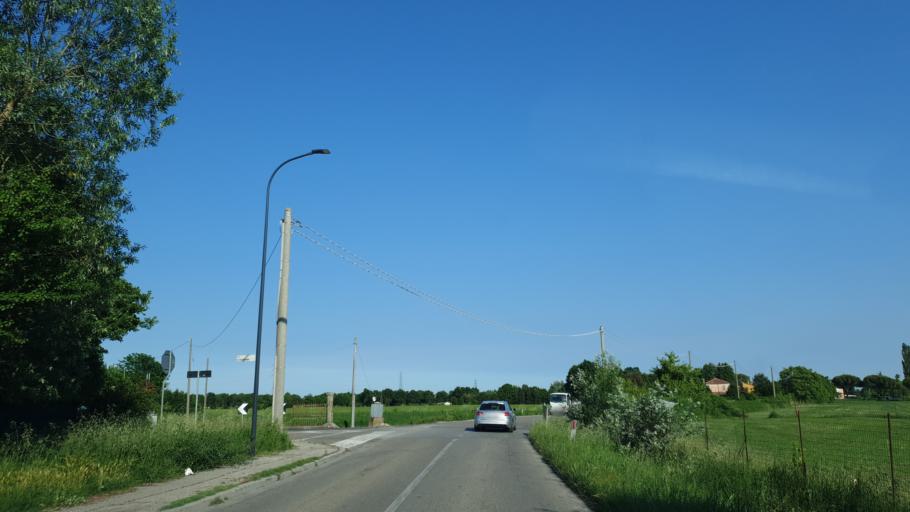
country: IT
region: Emilia-Romagna
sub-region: Provincia di Ravenna
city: Ravenna
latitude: 44.4143
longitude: 12.2237
